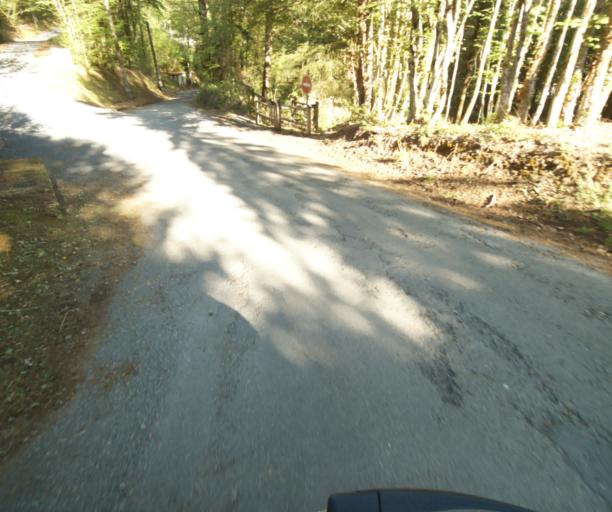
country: FR
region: Limousin
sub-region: Departement de la Correze
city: Tulle
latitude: 45.2601
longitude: 1.7698
